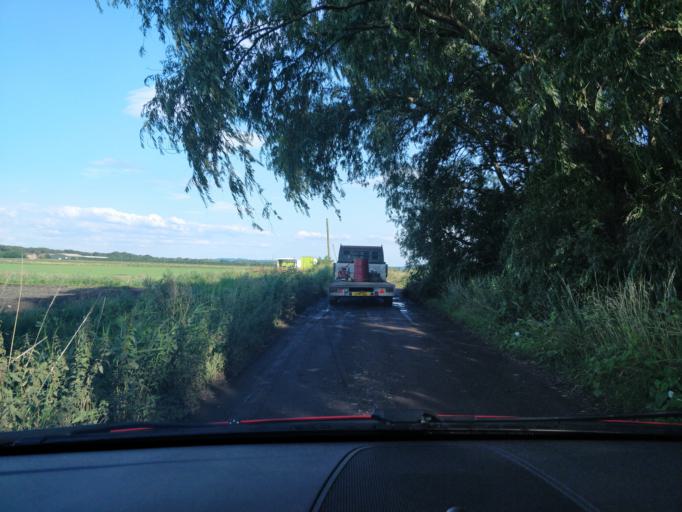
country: GB
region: England
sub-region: Lancashire
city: Banks
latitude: 53.6542
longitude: -2.9216
